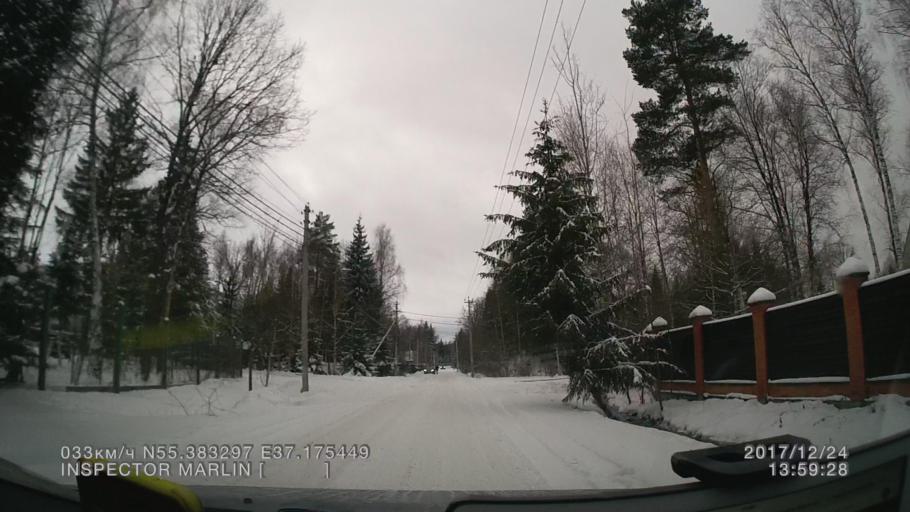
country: RU
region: Moskovskaya
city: Troitsk
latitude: 55.3833
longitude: 37.1754
